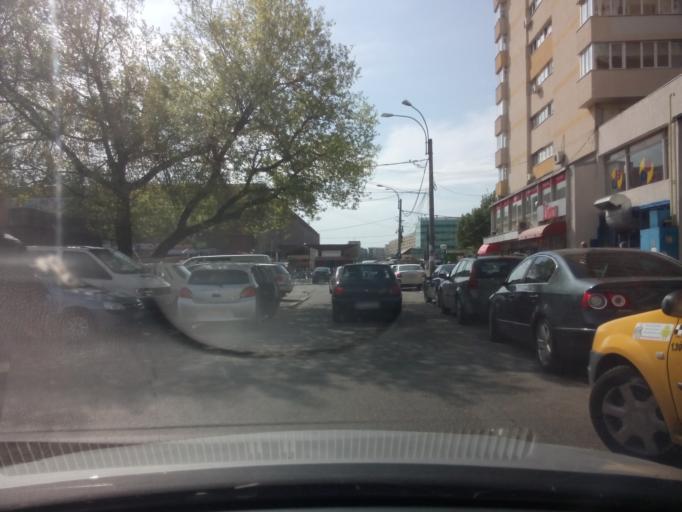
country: RO
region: Bucuresti
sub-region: Municipiul Bucuresti
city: Bucharest
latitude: 44.4507
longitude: 26.1276
